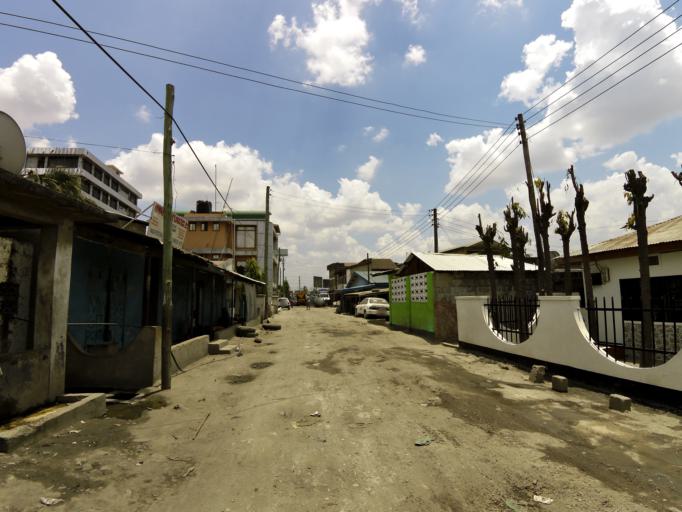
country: TZ
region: Dar es Salaam
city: Dar es Salaam
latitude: -6.8359
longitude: 39.2430
